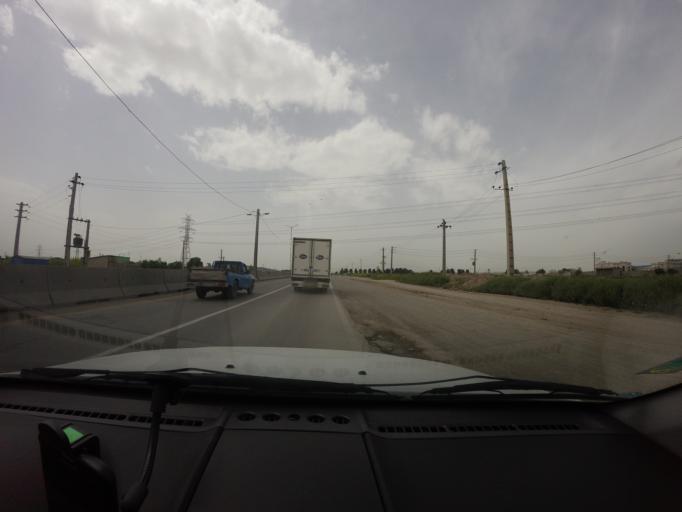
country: IR
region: Tehran
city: Eslamshahr
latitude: 35.5112
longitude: 51.2622
